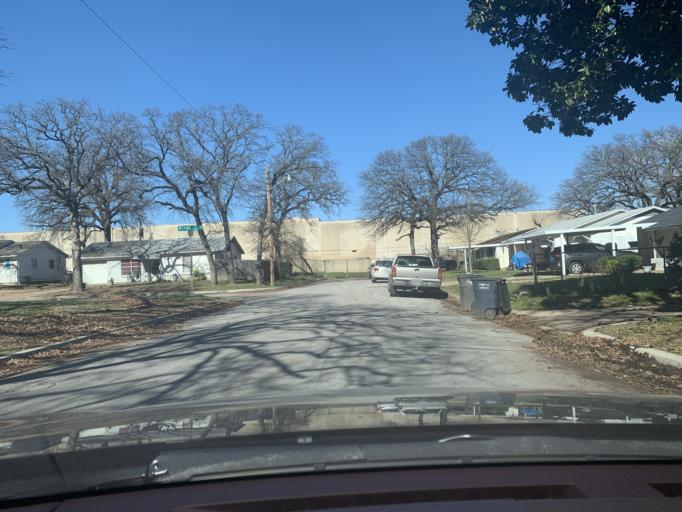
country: US
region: Texas
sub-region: Tarrant County
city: Haltom City
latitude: 32.7701
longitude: -97.2825
